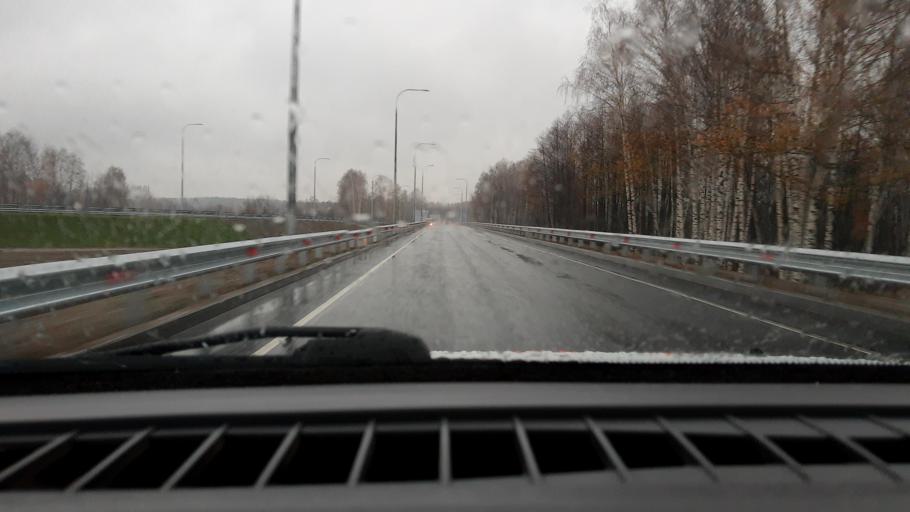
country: RU
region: Nizjnij Novgorod
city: Neklyudovo
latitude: 56.4244
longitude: 43.9924
